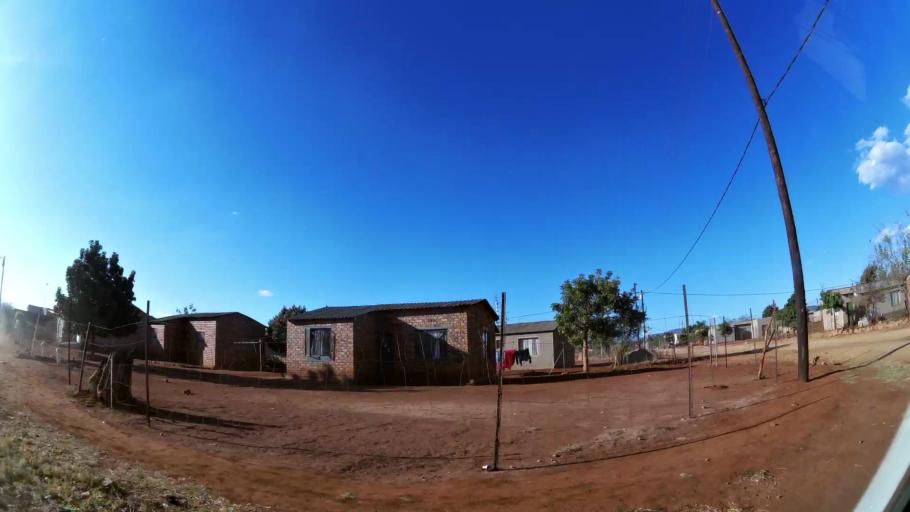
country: ZA
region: Limpopo
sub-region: Waterberg District Municipality
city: Mokopane
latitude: -24.1860
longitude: 28.9721
